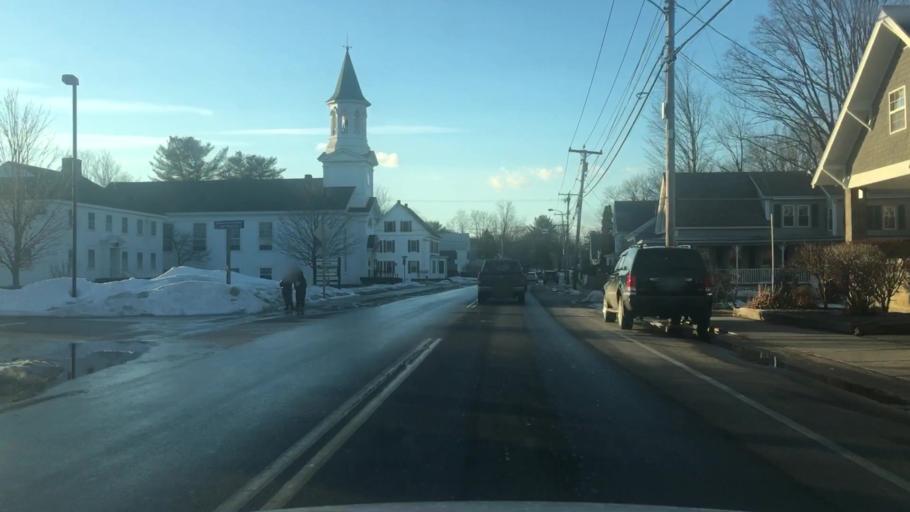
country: US
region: Maine
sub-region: York County
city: Springvale
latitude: 43.4672
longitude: -70.7987
